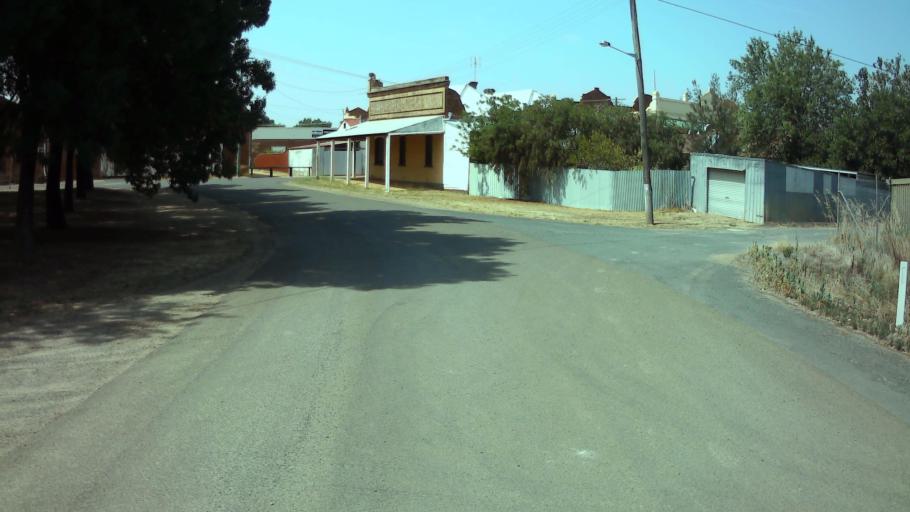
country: AU
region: New South Wales
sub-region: Weddin
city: Grenfell
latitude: -33.8930
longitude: 148.1584
